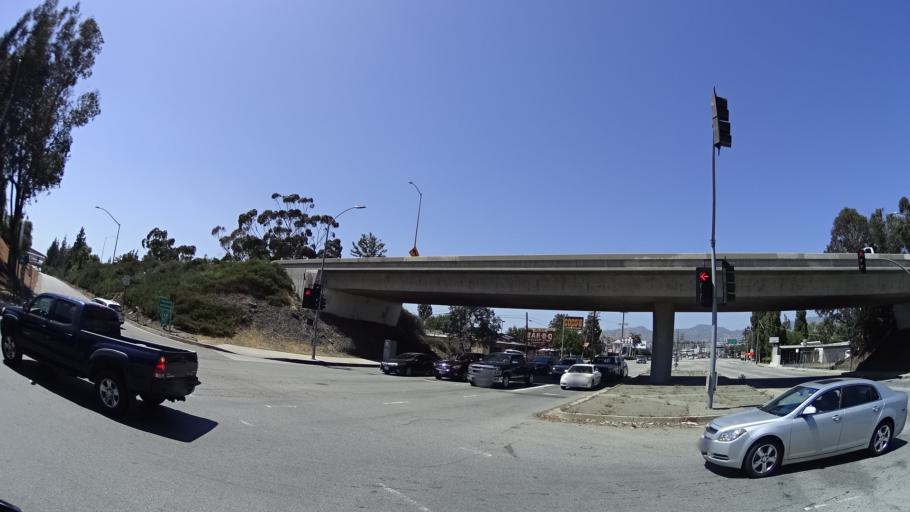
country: US
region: California
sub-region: Los Angeles County
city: San Fernando
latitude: 34.2663
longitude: -118.4672
